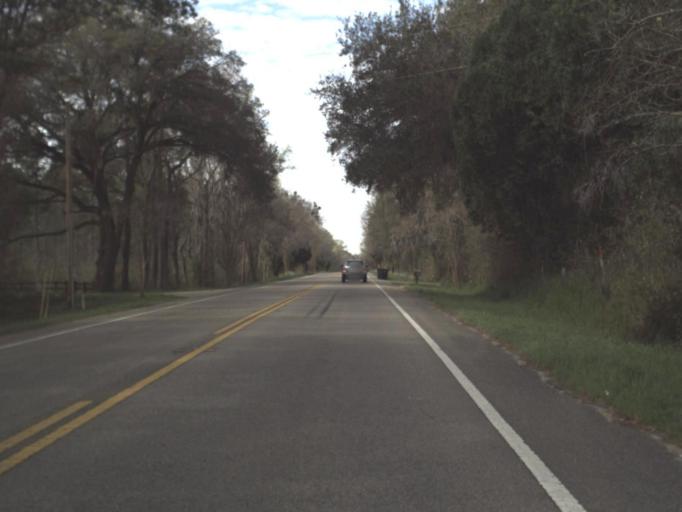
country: US
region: Florida
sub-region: Leon County
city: Tallahassee
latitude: 30.5006
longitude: -84.0997
